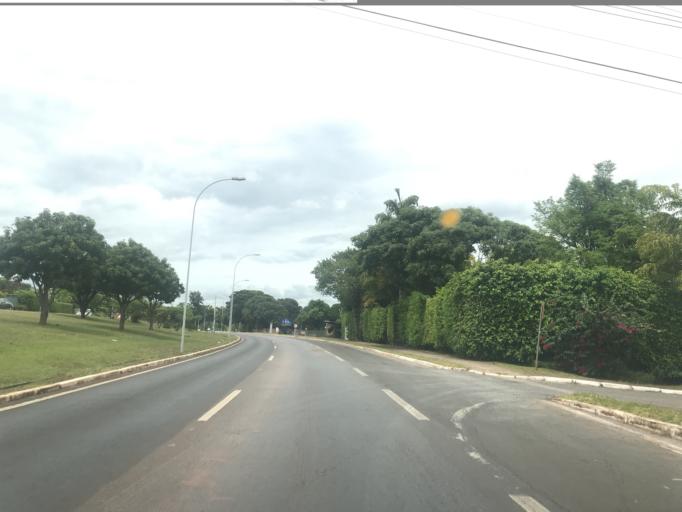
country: BR
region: Federal District
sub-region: Brasilia
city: Brasilia
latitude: -15.8354
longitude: -47.8351
